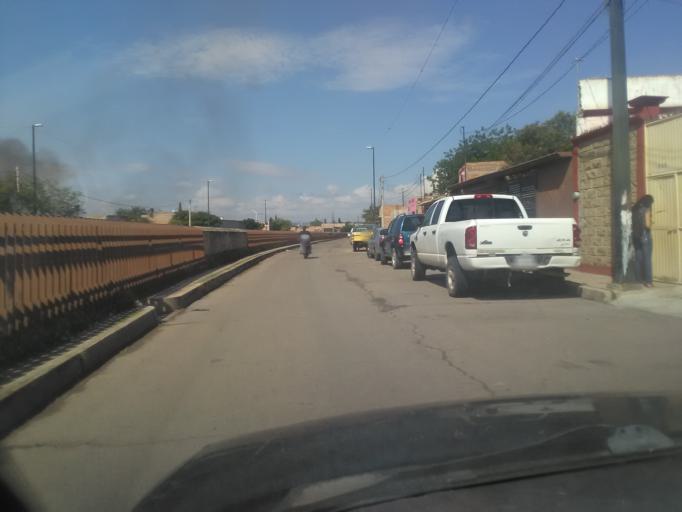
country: MX
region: Durango
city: Victoria de Durango
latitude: 24.0194
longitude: -104.6286
